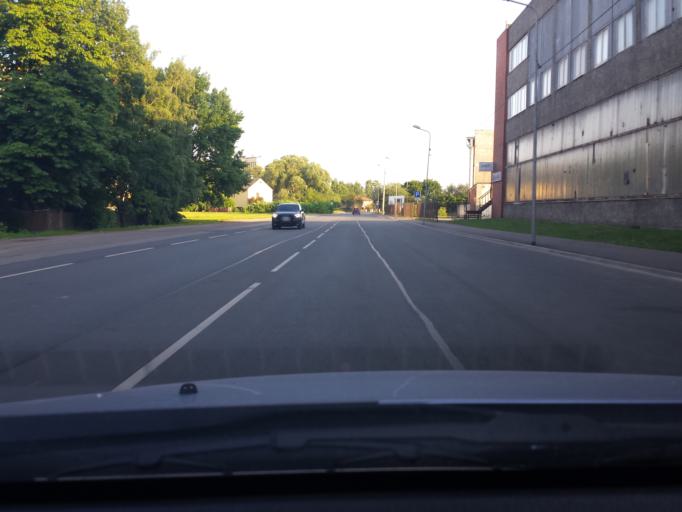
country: LV
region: Riga
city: Riga
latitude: 56.9583
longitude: 24.1655
